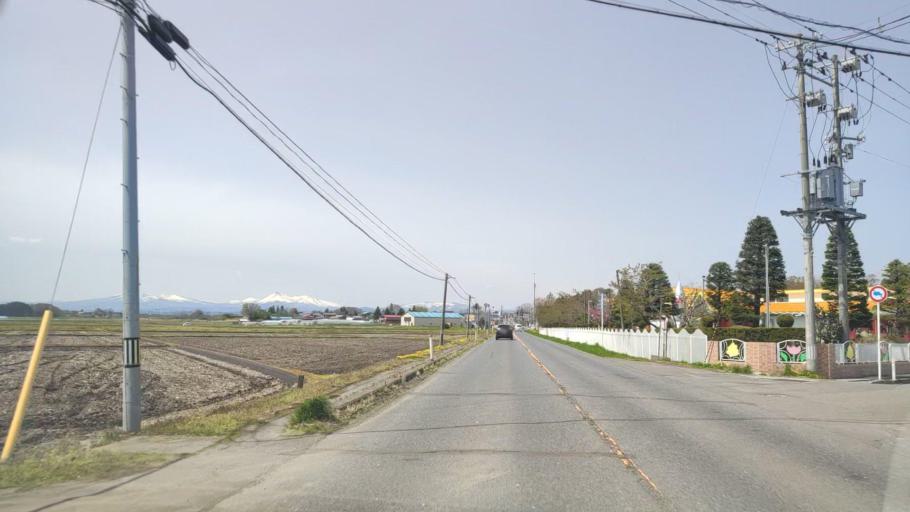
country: JP
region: Aomori
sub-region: Misawa Shi
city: Inuotose
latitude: 40.6040
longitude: 141.2955
